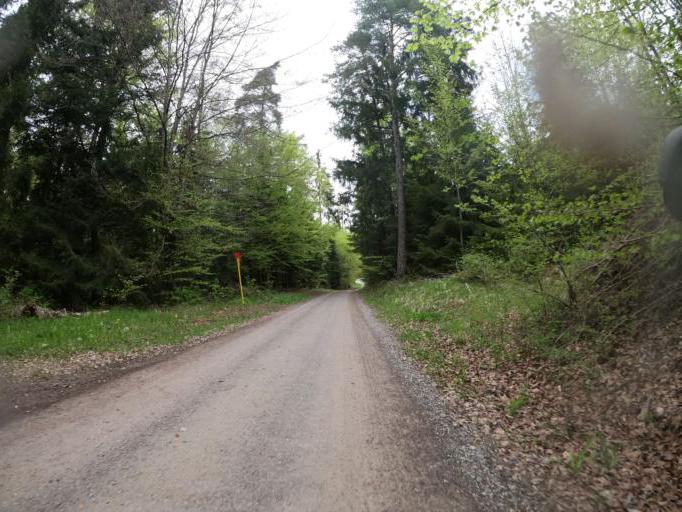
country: DE
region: Baden-Wuerttemberg
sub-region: Regierungsbezirk Stuttgart
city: Motzingen
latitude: 48.5475
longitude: 8.7597
